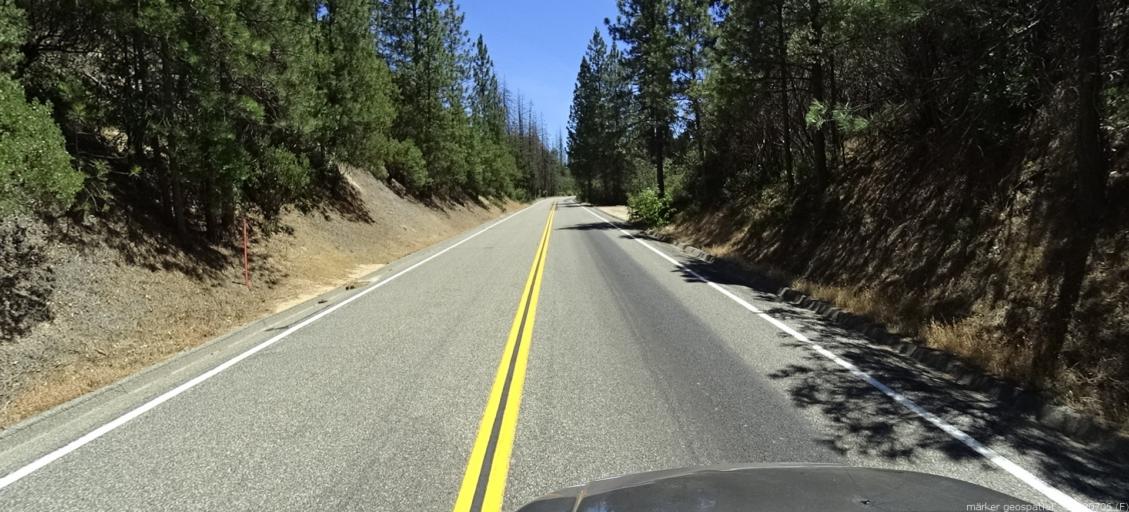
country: US
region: California
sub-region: Madera County
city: Oakhurst
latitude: 37.2915
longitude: -119.5208
